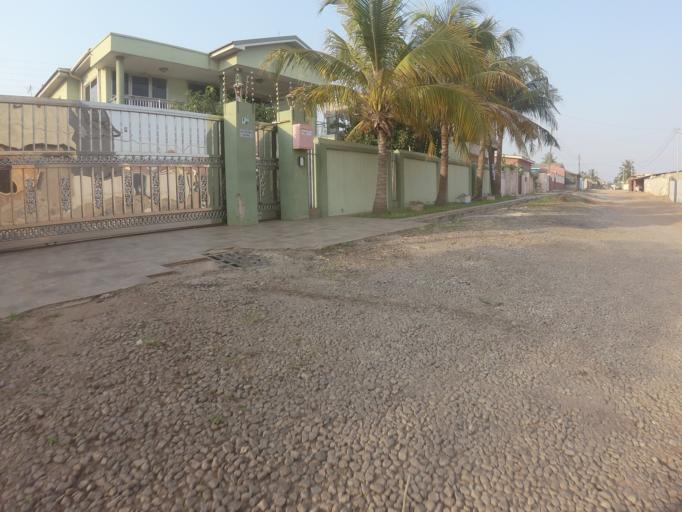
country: GH
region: Greater Accra
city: Nungua
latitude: 5.6261
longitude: -0.0635
